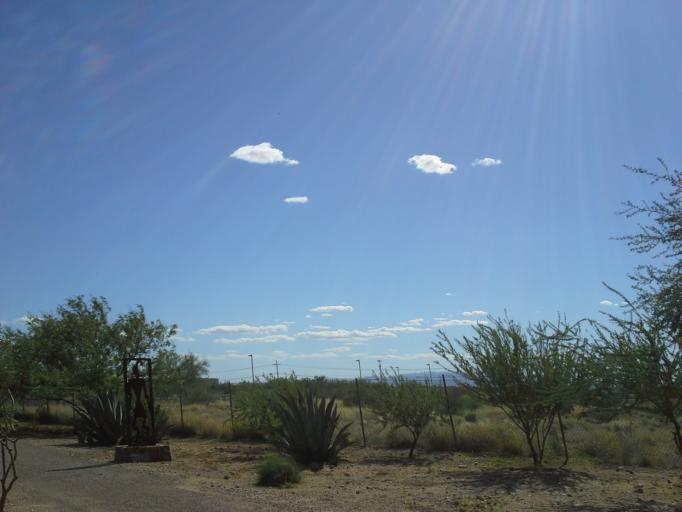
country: US
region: Arizona
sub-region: Pima County
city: Summit
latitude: 32.1165
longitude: -110.8394
